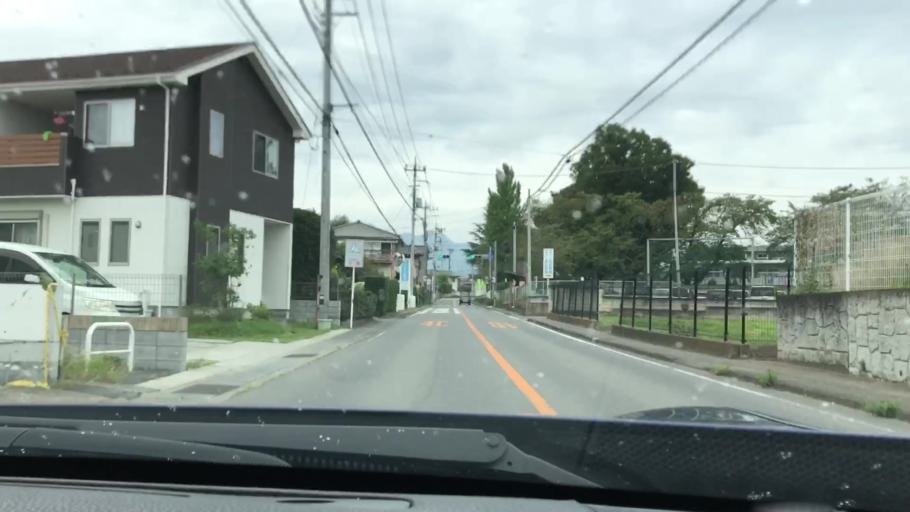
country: JP
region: Gunma
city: Kanekomachi
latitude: 36.3867
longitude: 138.9834
